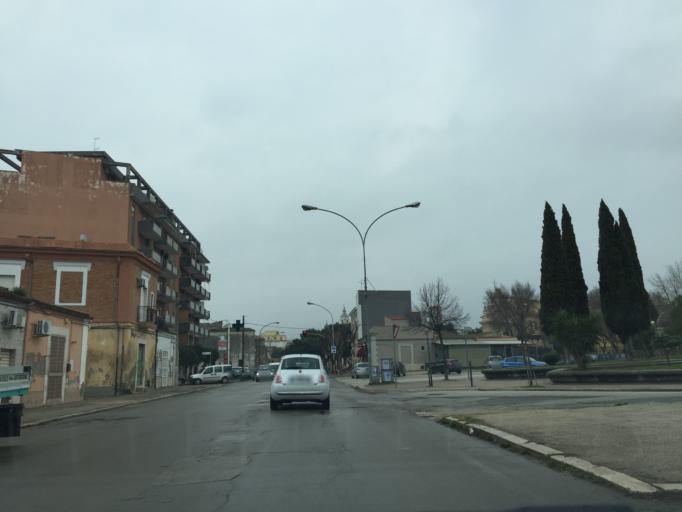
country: IT
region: Apulia
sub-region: Provincia di Foggia
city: Foggia
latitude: 41.4676
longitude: 15.5410
